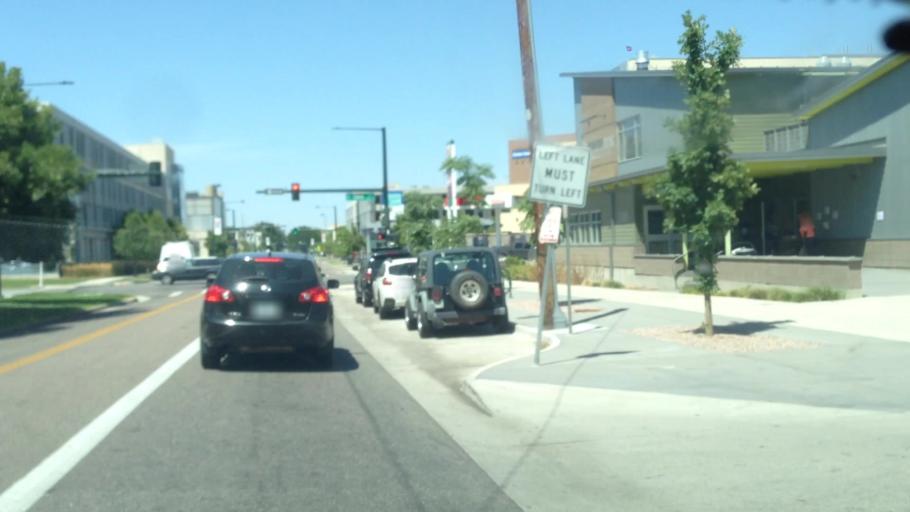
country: US
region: Colorado
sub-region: Denver County
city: Denver
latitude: 39.7443
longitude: -104.9734
